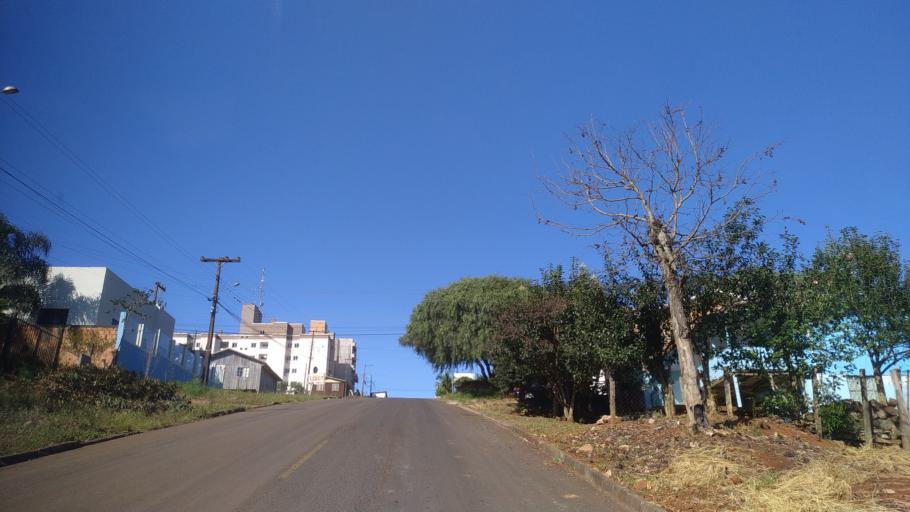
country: BR
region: Santa Catarina
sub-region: Chapeco
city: Chapeco
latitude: -27.1185
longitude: -52.5939
